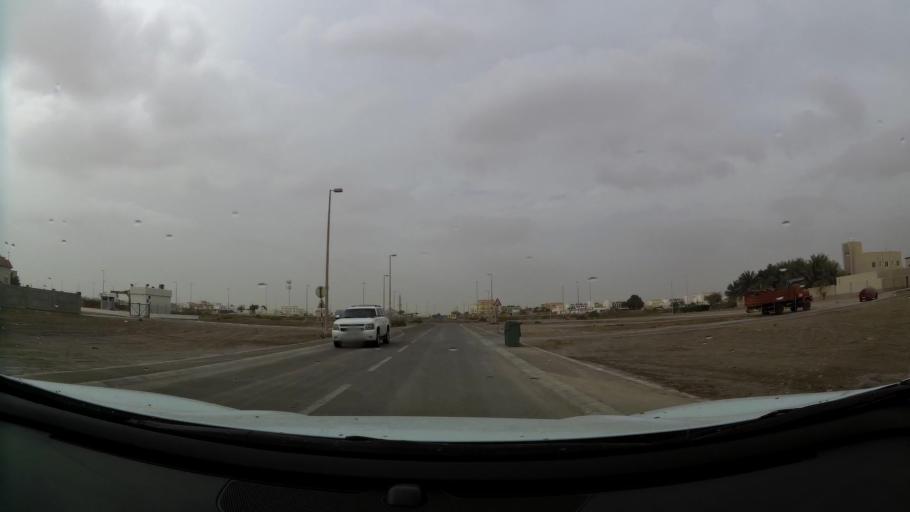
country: AE
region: Abu Dhabi
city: Abu Dhabi
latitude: 24.3586
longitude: 54.6599
